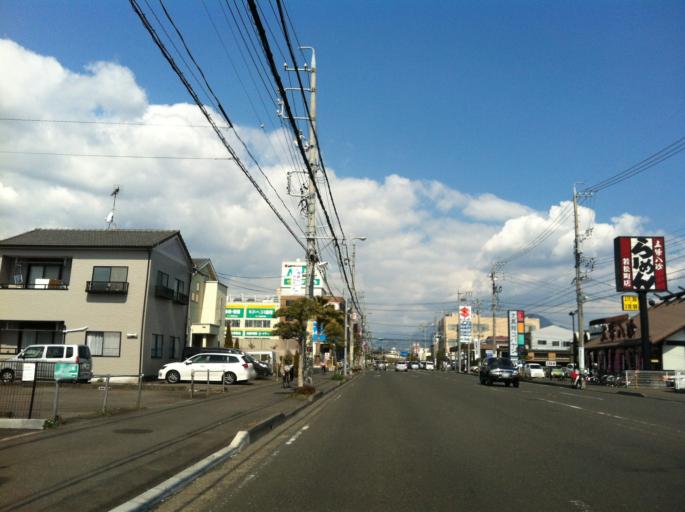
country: JP
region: Shizuoka
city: Shizuoka-shi
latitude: 34.9828
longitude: 138.3661
